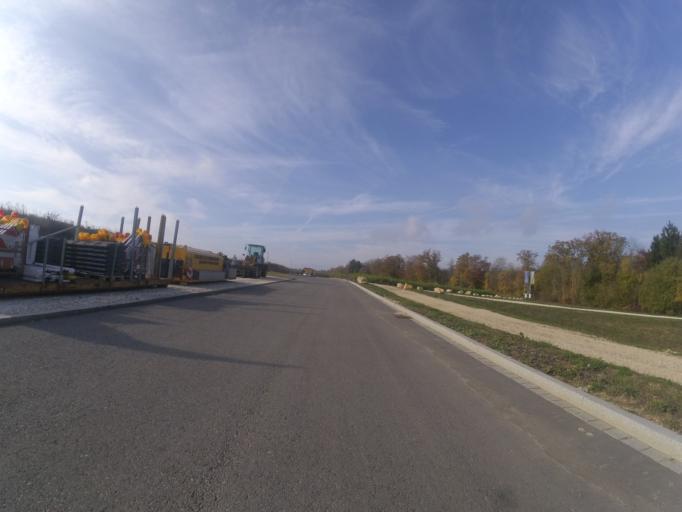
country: DE
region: Baden-Wuerttemberg
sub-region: Tuebingen Region
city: Dornstadt
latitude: 48.4264
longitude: 9.9325
